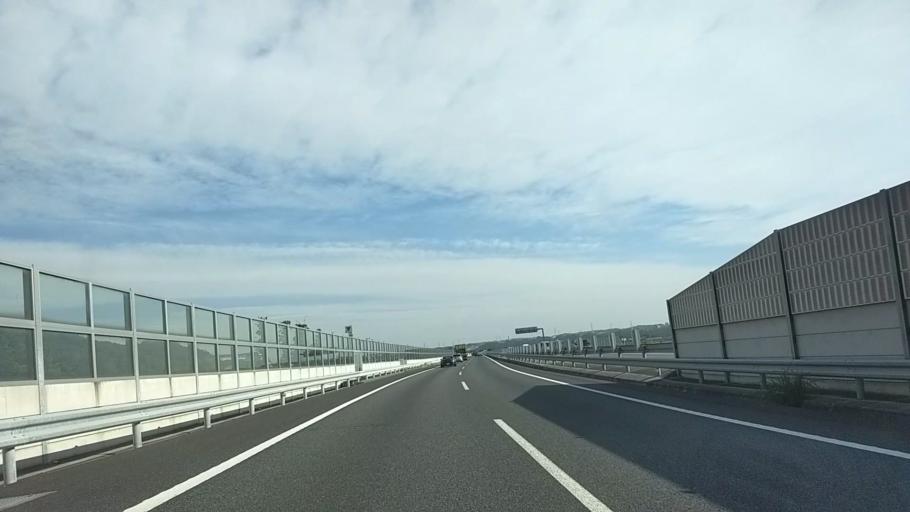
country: JP
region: Kanagawa
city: Zama
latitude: 35.5015
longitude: 139.3657
